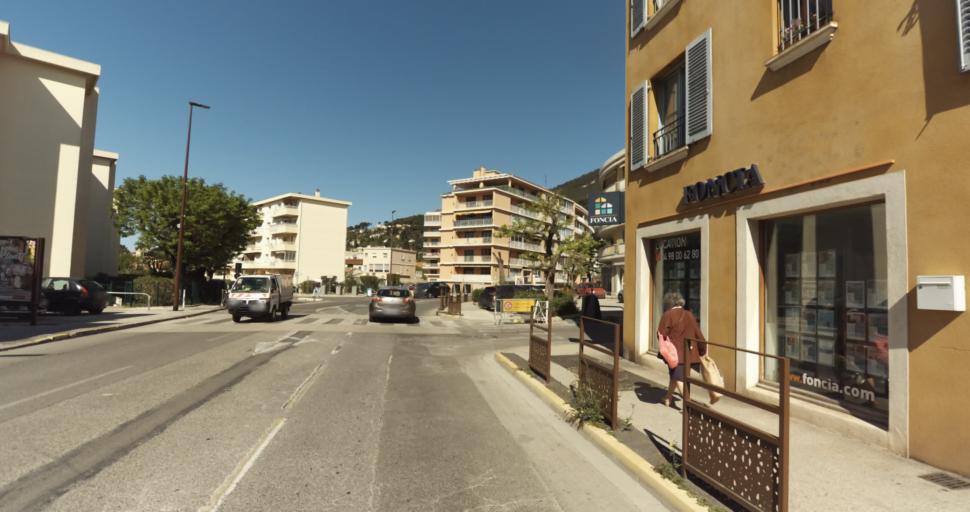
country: FR
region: Provence-Alpes-Cote d'Azur
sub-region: Departement du Var
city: La Valette-du-Var
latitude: 43.1361
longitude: 5.9824
